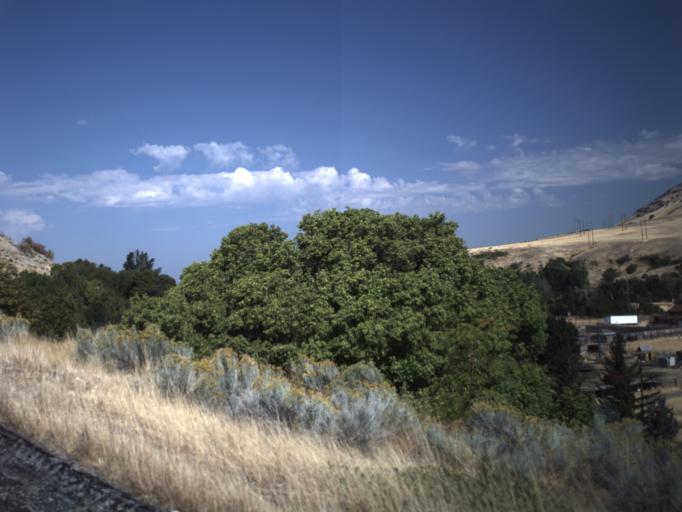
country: US
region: Utah
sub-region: Cache County
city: Hyrum
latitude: 41.6317
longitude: -111.8113
